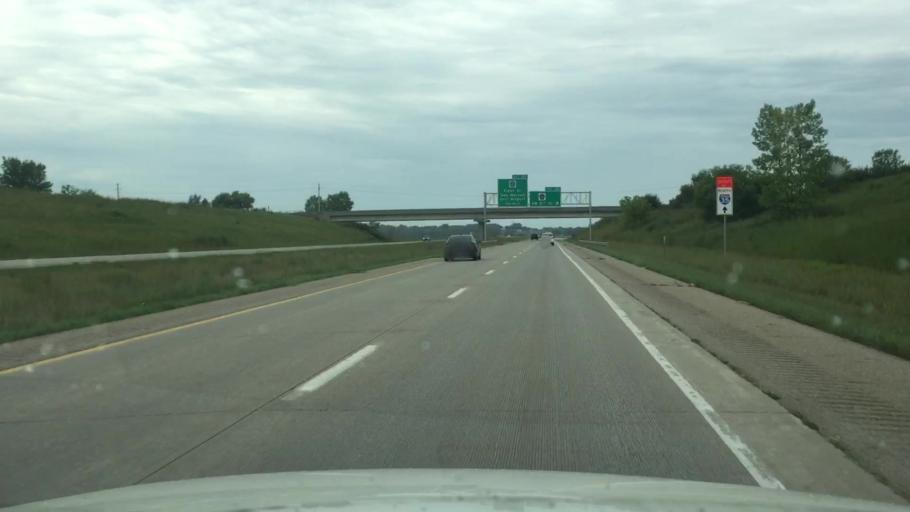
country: US
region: Iowa
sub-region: Warren County
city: Norwalk
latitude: 41.4983
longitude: -93.6136
